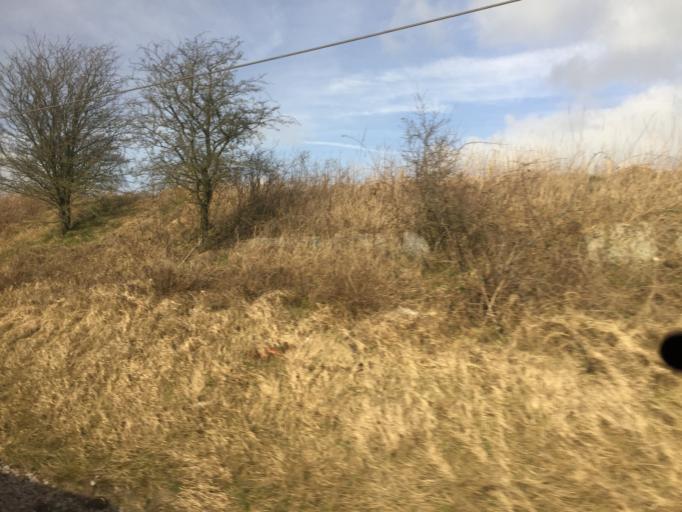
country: GB
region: Scotland
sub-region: Dumfries and Galloway
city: Annan
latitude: 55.0648
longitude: -3.2493
